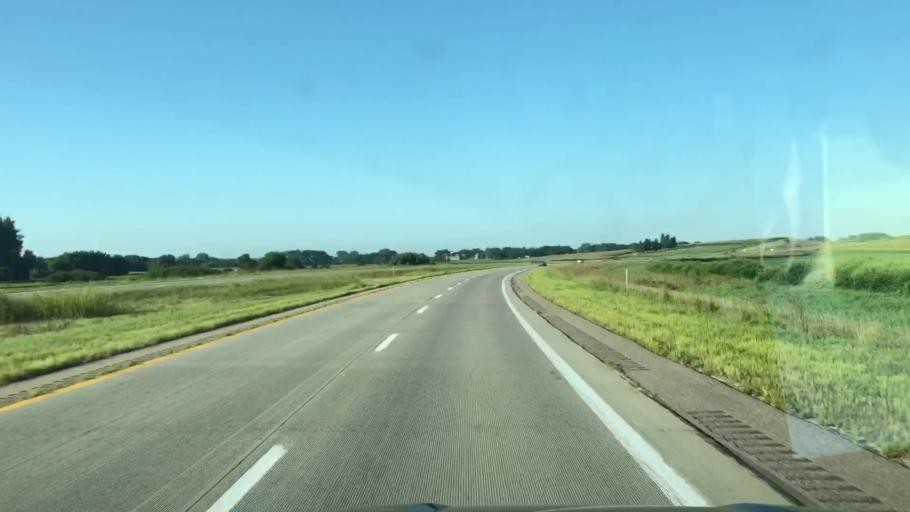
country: US
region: Iowa
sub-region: Plymouth County
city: Le Mars
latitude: 42.8642
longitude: -96.1175
